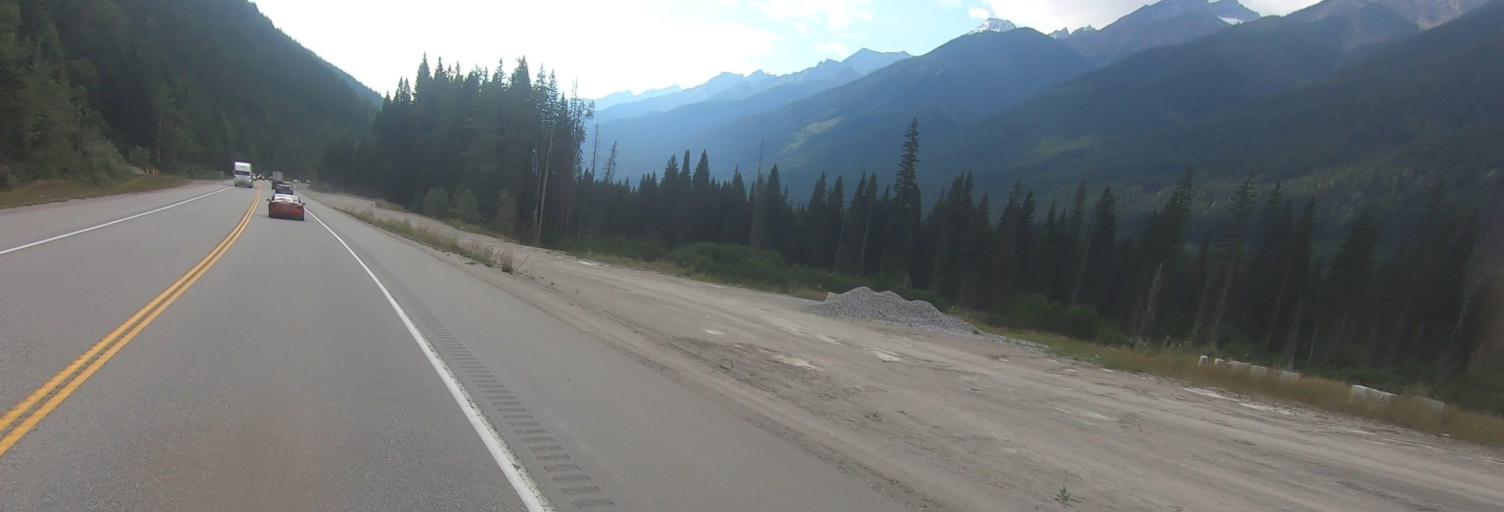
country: CA
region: British Columbia
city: Golden
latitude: 51.4306
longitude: -117.4783
